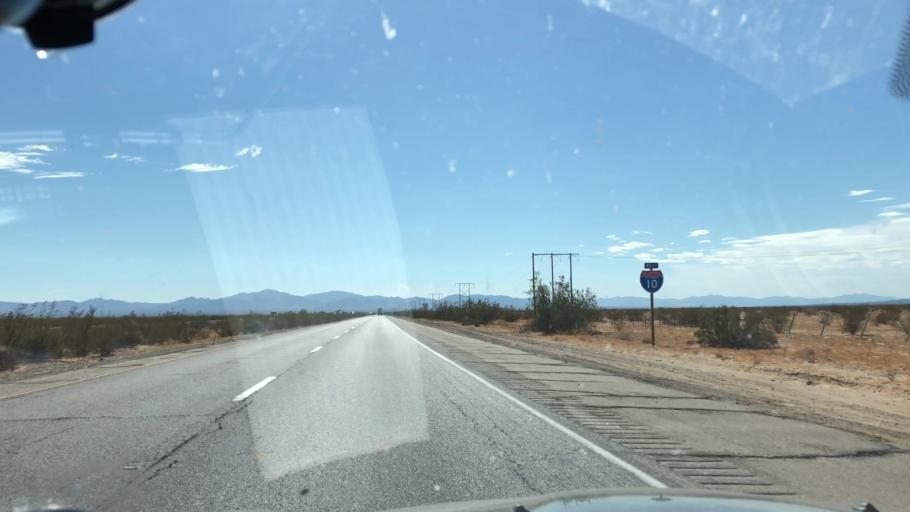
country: US
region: California
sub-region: Riverside County
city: Mesa Verde
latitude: 33.6062
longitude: -114.9265
